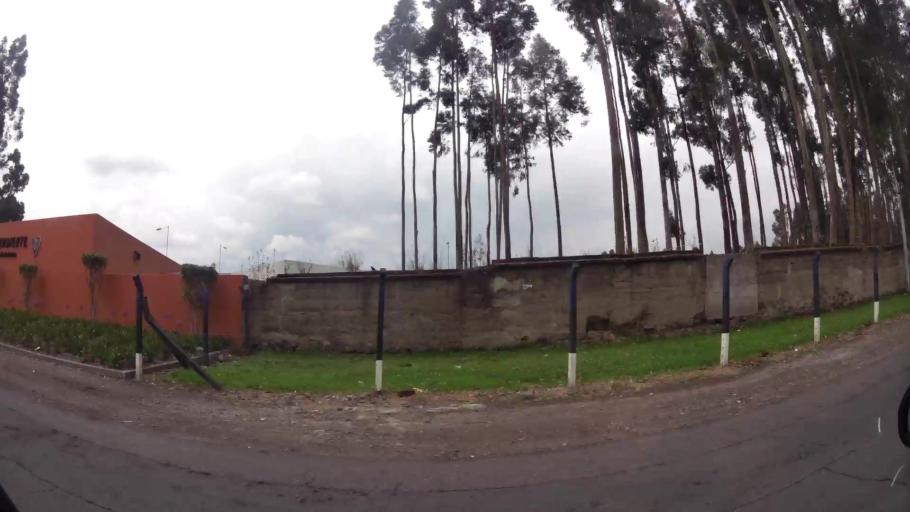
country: EC
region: Pichincha
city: Sangolqui
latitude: -0.3473
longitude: -78.4710
